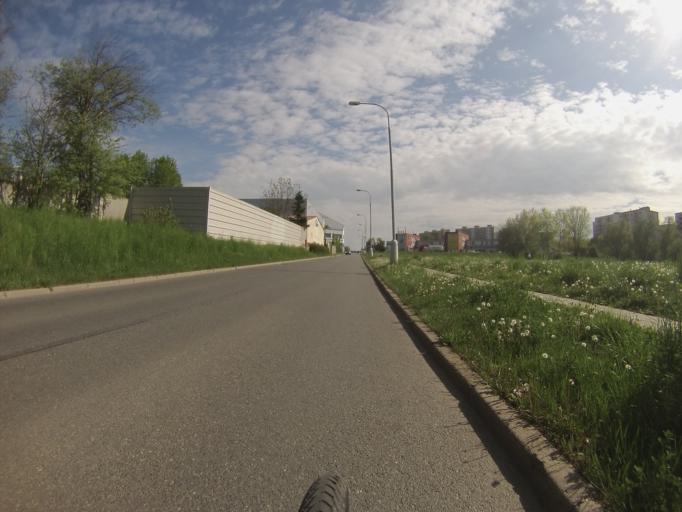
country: CZ
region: South Moravian
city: Troubsko
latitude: 49.2234
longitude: 16.5192
